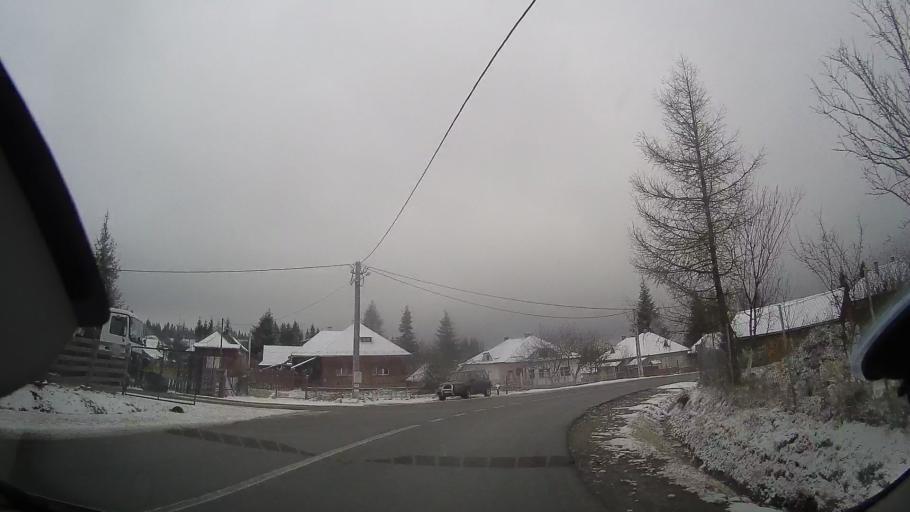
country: RO
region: Cluj
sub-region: Comuna Belis
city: Belis
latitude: 46.6817
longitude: 23.0339
